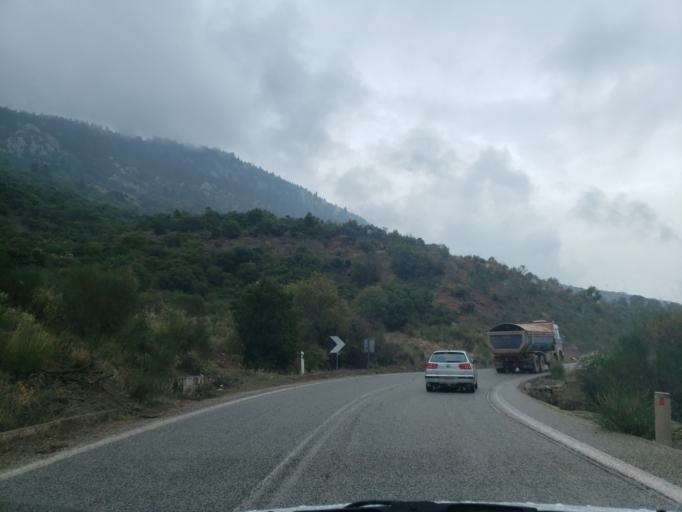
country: GR
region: Central Greece
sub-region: Nomos Fokidos
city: Amfissa
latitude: 38.5867
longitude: 22.3900
